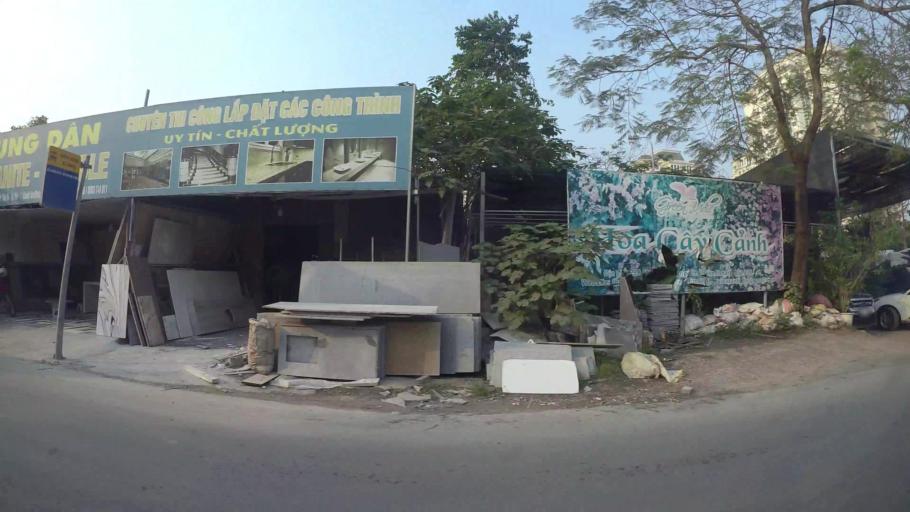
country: VN
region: Ha Noi
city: Tay Ho
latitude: 21.0774
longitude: 105.7909
